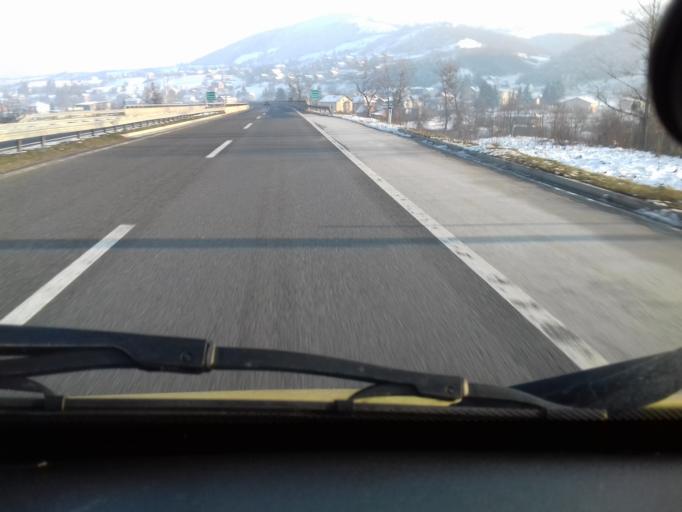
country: BA
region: Federation of Bosnia and Herzegovina
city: Visoko
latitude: 43.9930
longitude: 18.1942
